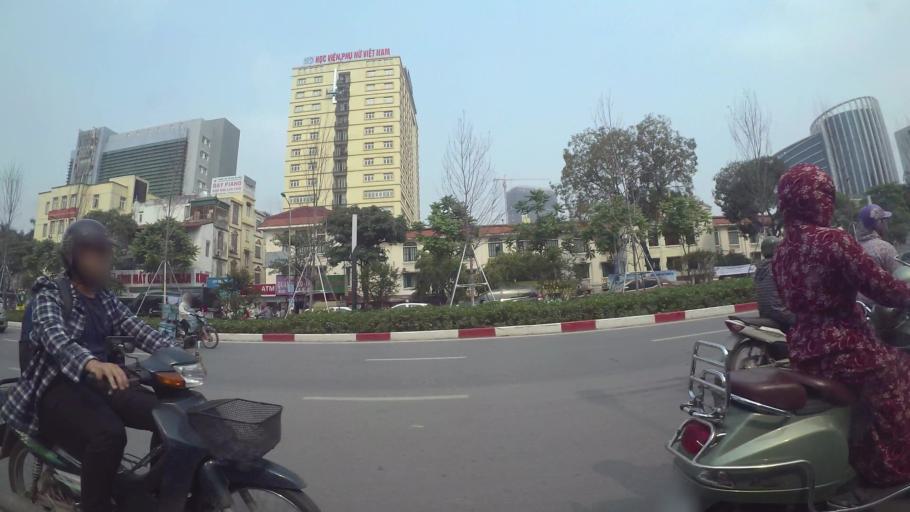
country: VN
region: Ha Noi
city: Cau Giay
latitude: 21.0189
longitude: 105.8078
